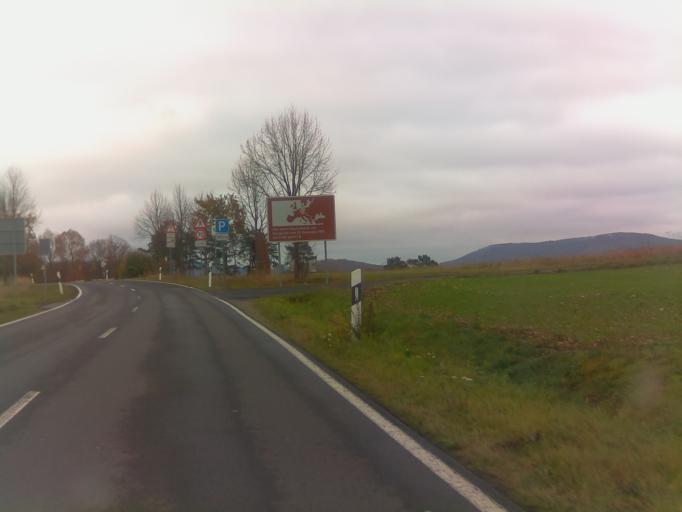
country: DE
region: Hesse
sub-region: Regierungsbezirk Kassel
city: Rasdorf
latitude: 50.7190
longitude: 9.9254
